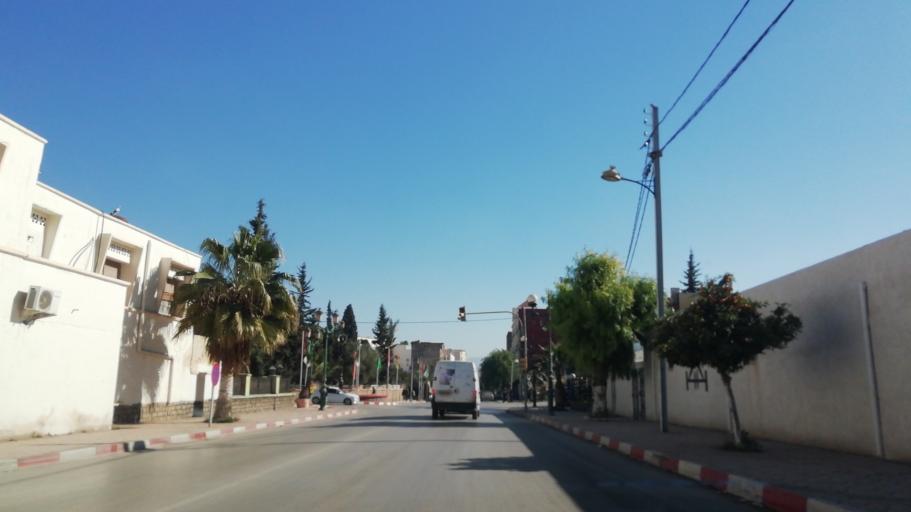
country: DZ
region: Tlemcen
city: Nedroma
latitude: 34.8464
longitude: -1.7278
